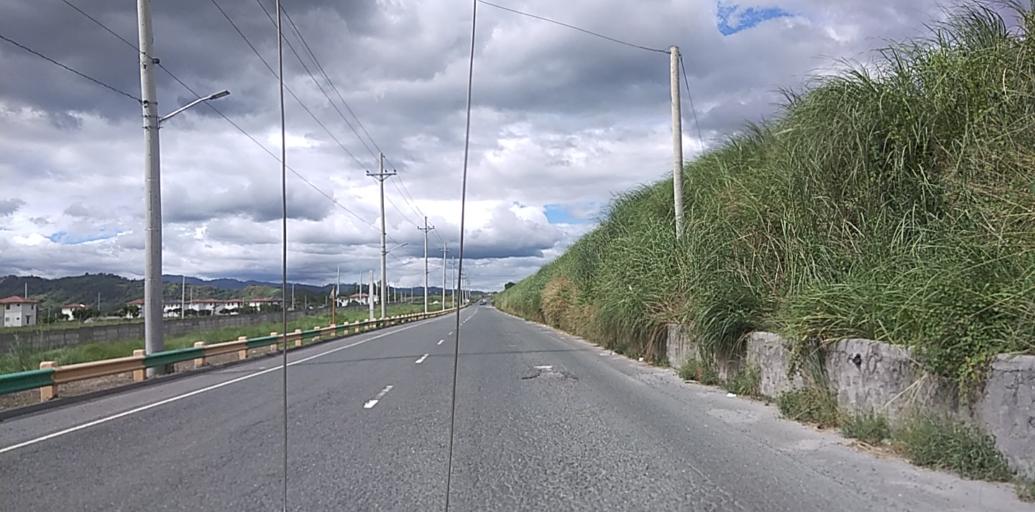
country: PH
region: Central Luzon
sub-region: Province of Pampanga
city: Dolores
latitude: 15.1130
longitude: 120.5168
